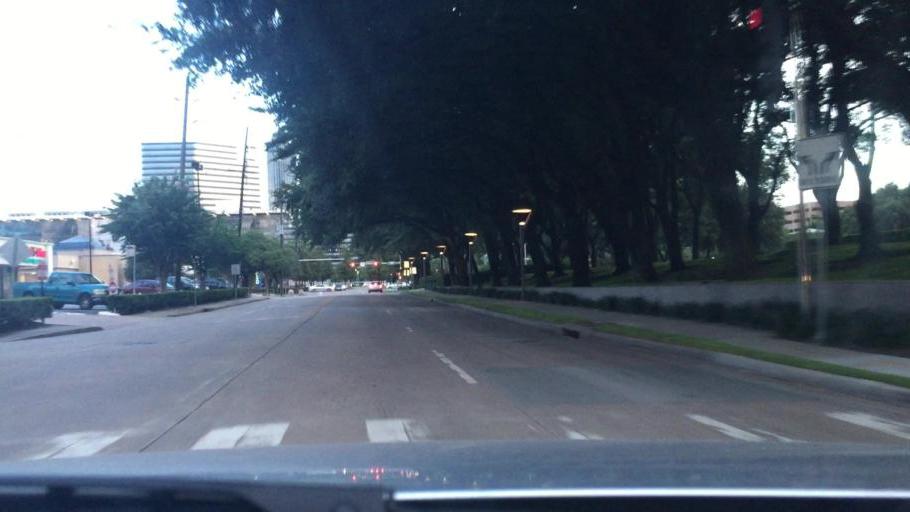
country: US
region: Texas
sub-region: Harris County
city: Hunters Creek Village
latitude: 29.7519
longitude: -95.4630
